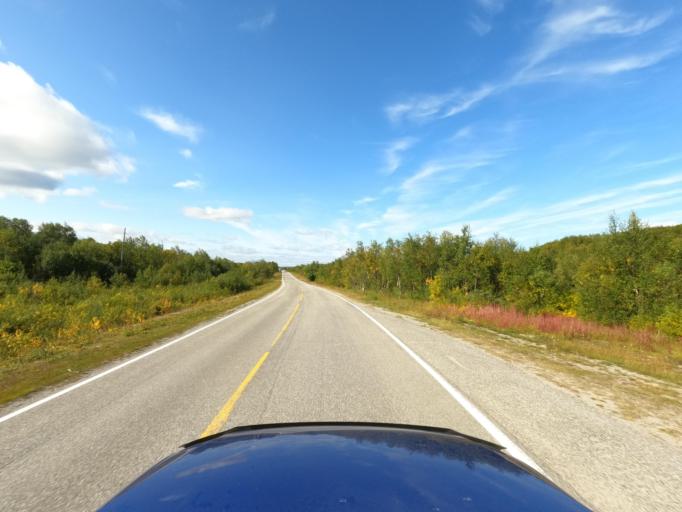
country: NO
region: Finnmark Fylke
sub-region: Porsanger
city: Lakselv
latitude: 69.7630
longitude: 25.1979
